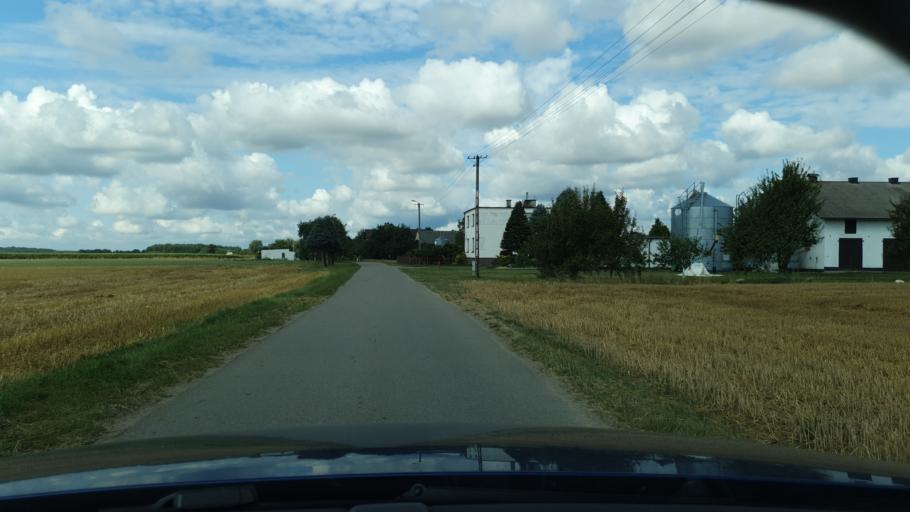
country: PL
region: Pomeranian Voivodeship
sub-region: Powiat czluchowski
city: Przechlewo
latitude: 53.8094
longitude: 17.3847
